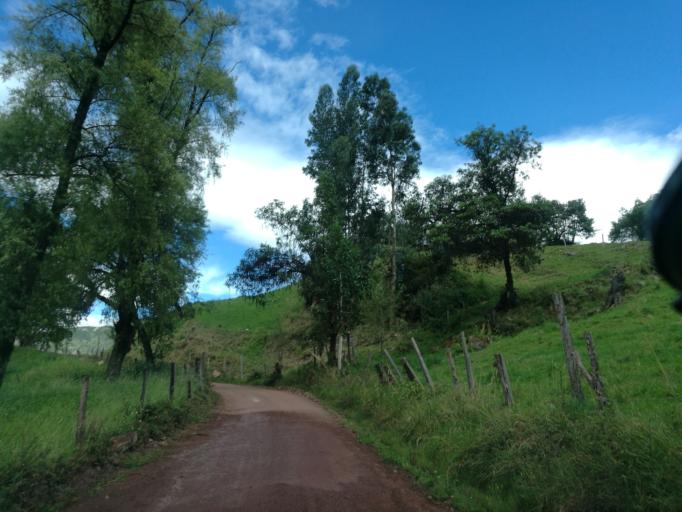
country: CO
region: Boyaca
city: Socota
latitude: 6.1117
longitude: -72.7178
